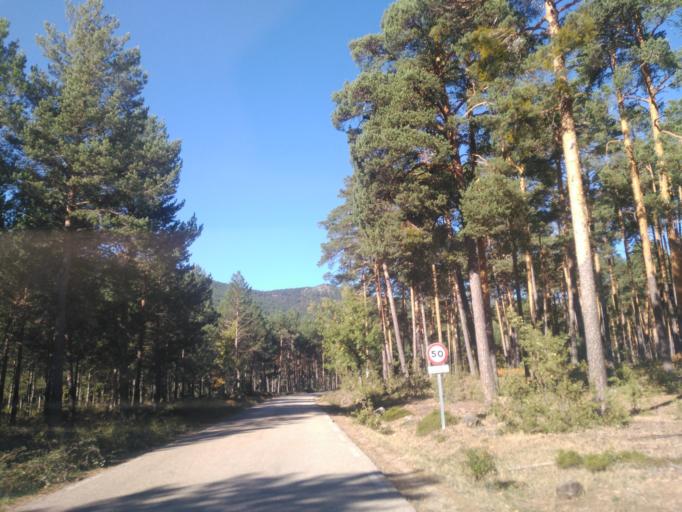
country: ES
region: Castille and Leon
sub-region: Provincia de Soria
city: Vinuesa
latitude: 41.9753
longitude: -2.7879
